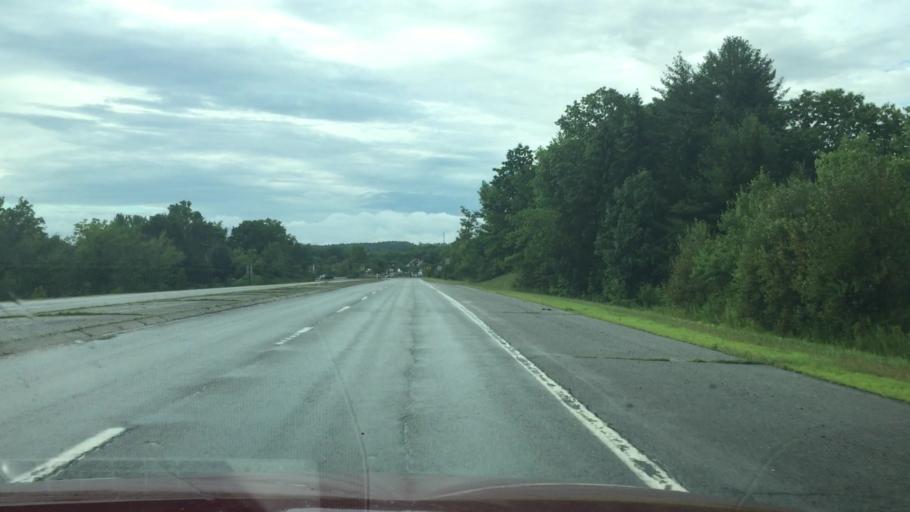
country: US
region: Maine
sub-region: Cumberland County
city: Westbrook
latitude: 43.6754
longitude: -70.3525
